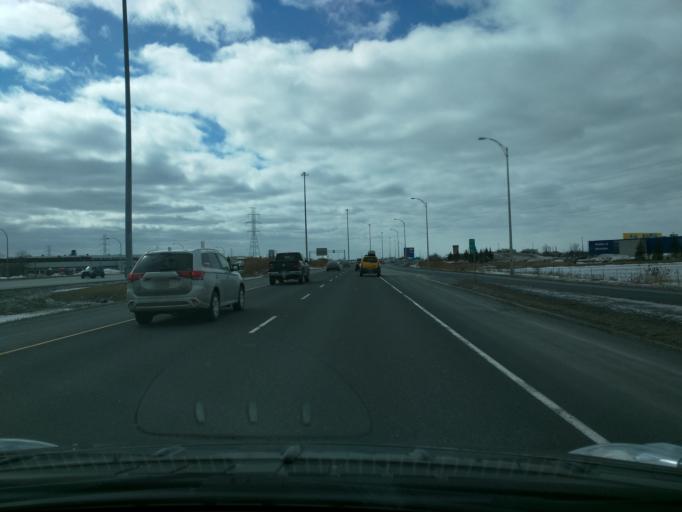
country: CA
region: Quebec
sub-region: Monteregie
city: Boucherville
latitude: 45.5708
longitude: -73.3958
